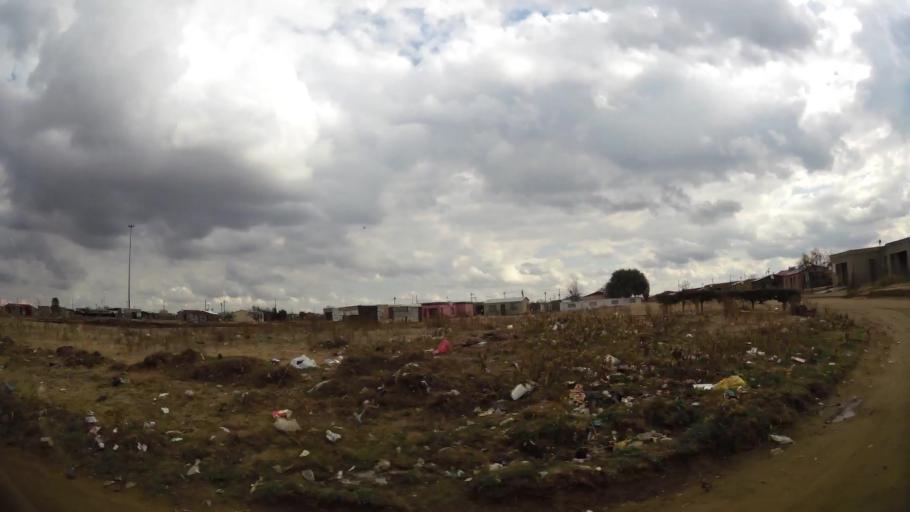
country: ZA
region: Orange Free State
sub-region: Fezile Dabi District Municipality
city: Sasolburg
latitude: -26.8630
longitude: 27.8647
